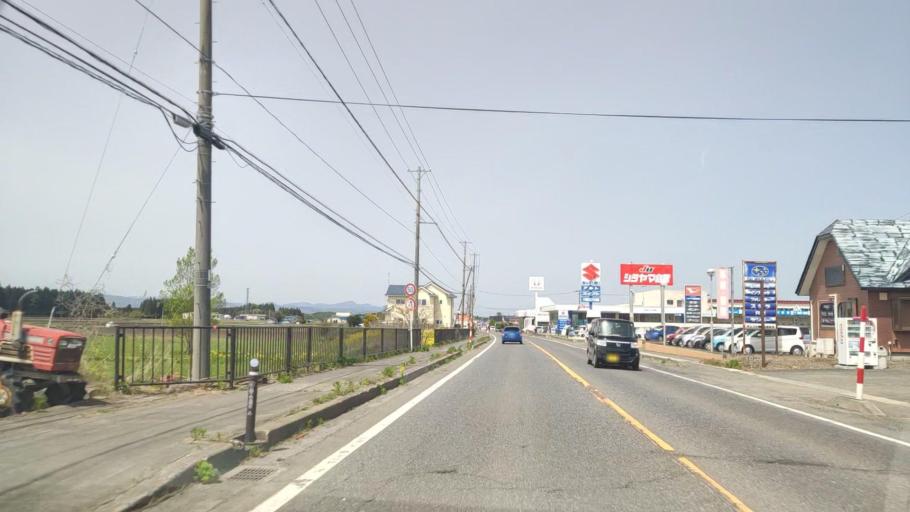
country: JP
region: Aomori
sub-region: Misawa Shi
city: Inuotose
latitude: 40.6498
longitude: 141.1963
